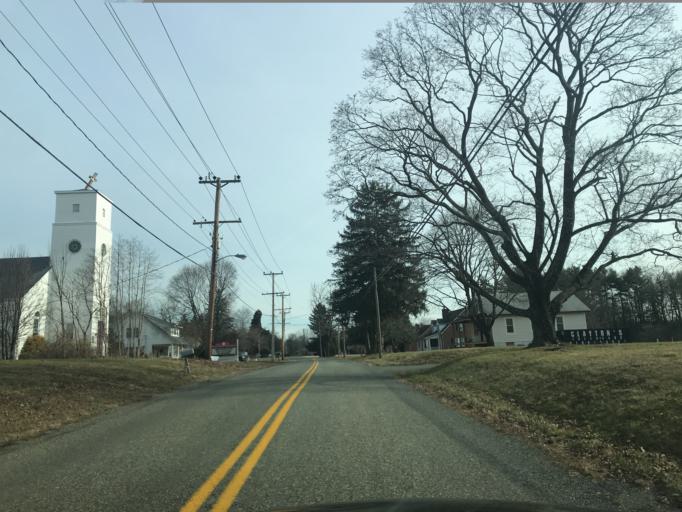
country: US
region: Maryland
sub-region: Harford County
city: Aberdeen
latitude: 39.5725
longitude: -76.1618
